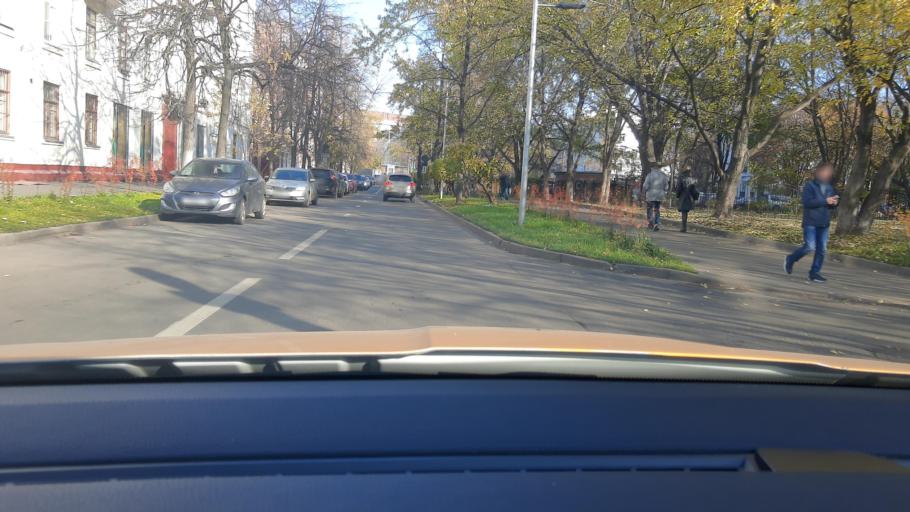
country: RU
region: Moscow
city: Novokuz'minki
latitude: 55.7153
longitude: 37.7827
